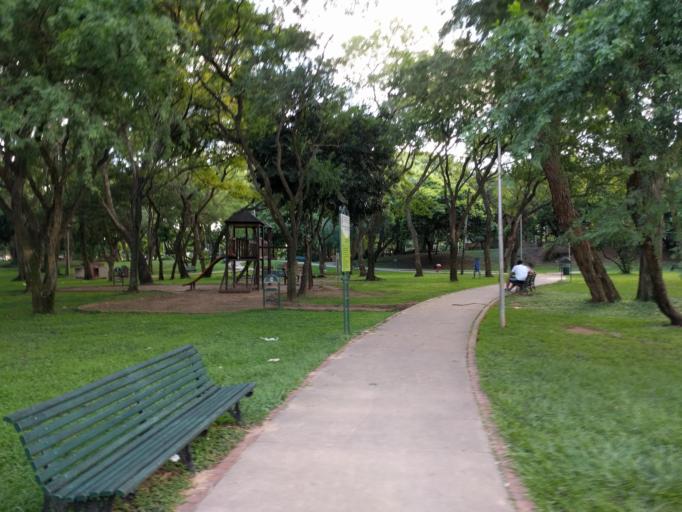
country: BO
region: Santa Cruz
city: Santa Cruz de la Sierra
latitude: -17.7810
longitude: -63.2171
